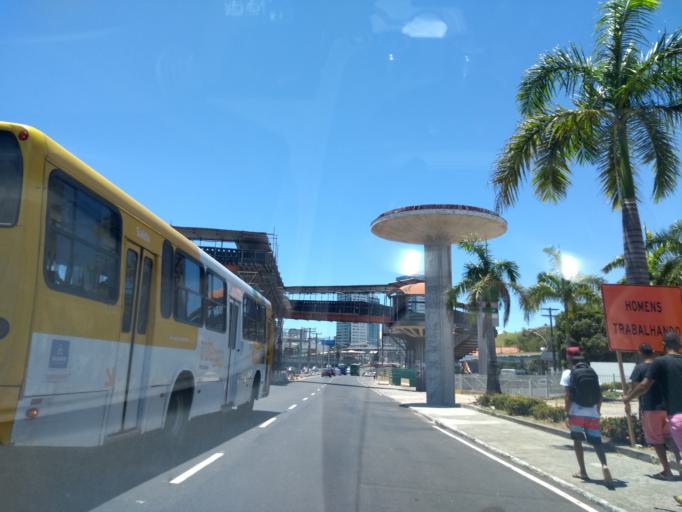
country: BR
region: Bahia
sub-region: Salvador
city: Salvador
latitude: -12.9747
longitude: -38.4524
